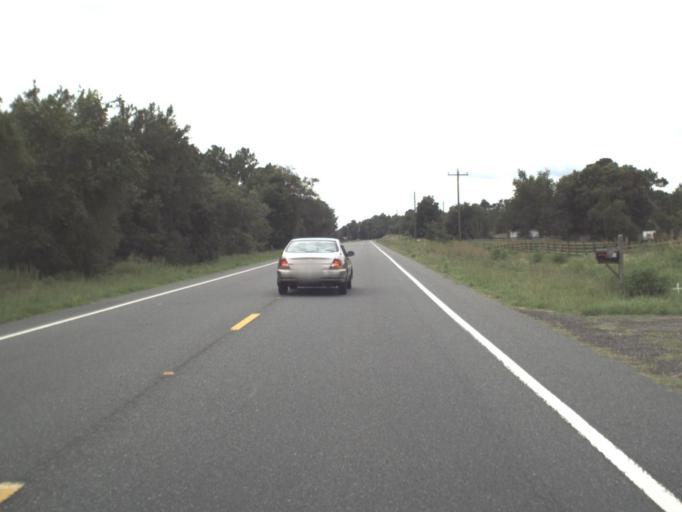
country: US
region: Florida
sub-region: Levy County
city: Williston Highlands
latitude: 29.2247
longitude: -82.4410
